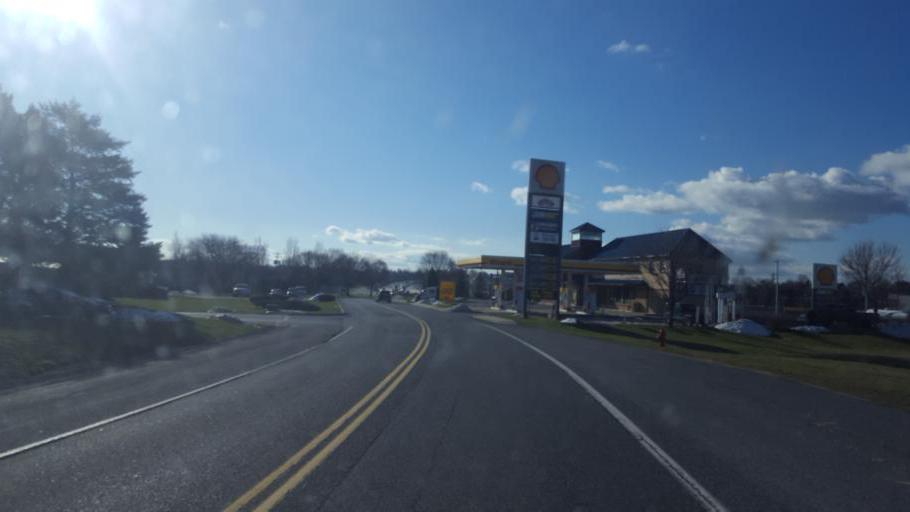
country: US
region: Pennsylvania
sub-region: Lancaster County
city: Lancaster
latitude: 40.0502
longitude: -76.2539
